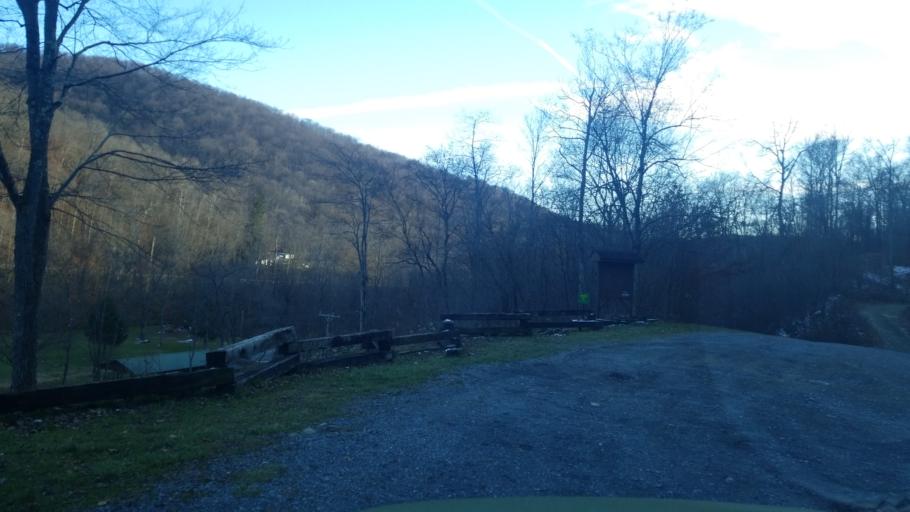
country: US
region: Pennsylvania
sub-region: Potter County
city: Coudersport
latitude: 41.6530
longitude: -78.0866
